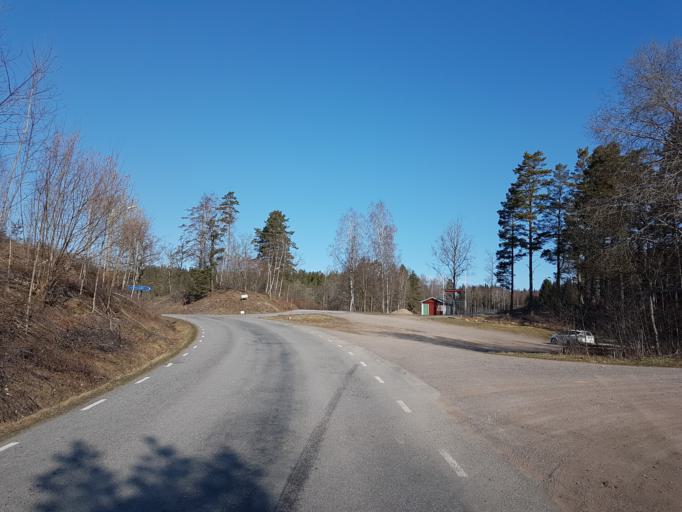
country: SE
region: OEstergoetland
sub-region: Valdemarsviks Kommun
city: Gusum
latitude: 58.1976
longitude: 16.3680
